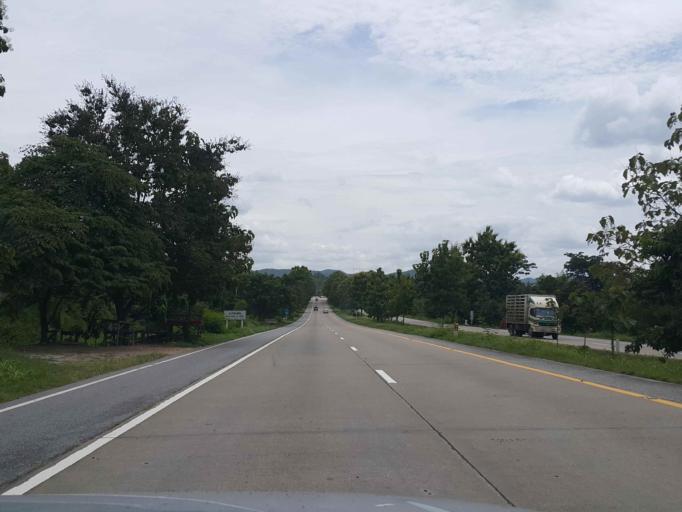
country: TH
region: Lamphun
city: Mae Tha
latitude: 18.4754
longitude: 99.1274
